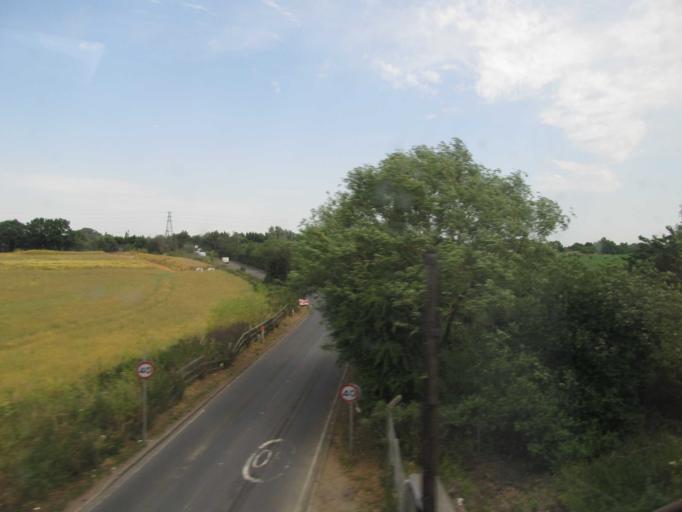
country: GB
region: England
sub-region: Surrey
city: Colnbrook
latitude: 51.5083
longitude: -0.5305
